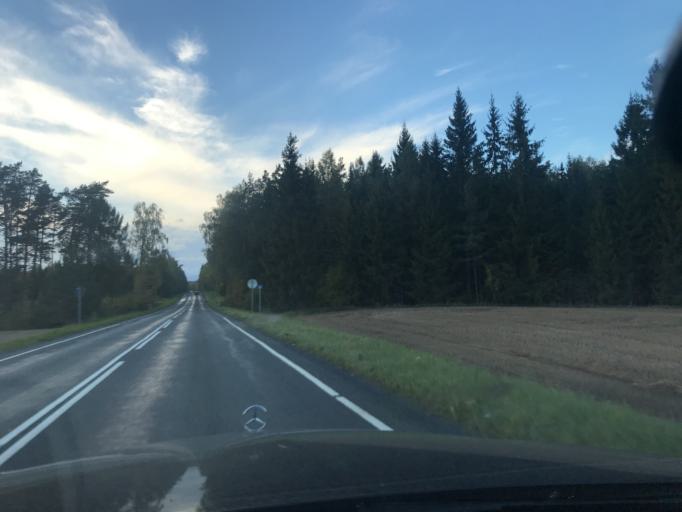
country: EE
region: Vorumaa
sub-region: Antsla vald
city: Vana-Antsla
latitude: 57.8730
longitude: 26.5920
